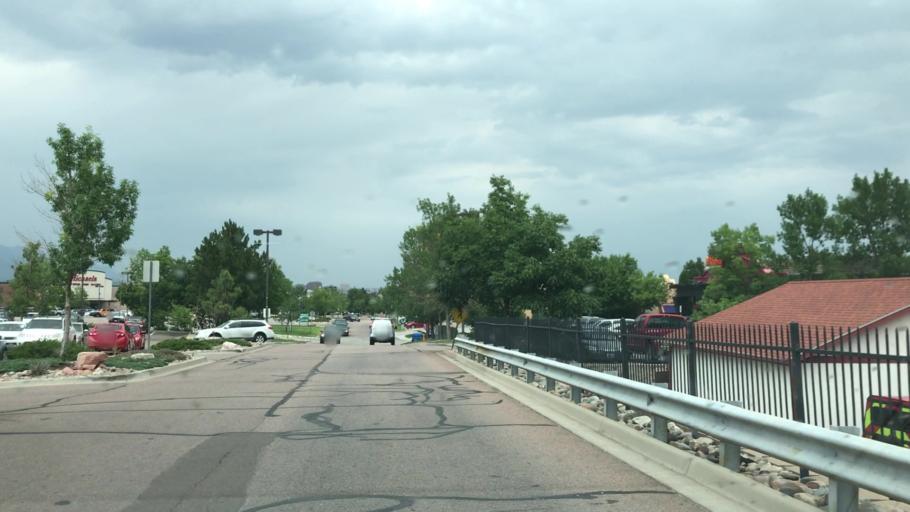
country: US
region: Colorado
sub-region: El Paso County
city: Colorado Springs
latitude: 38.7991
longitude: -104.8184
